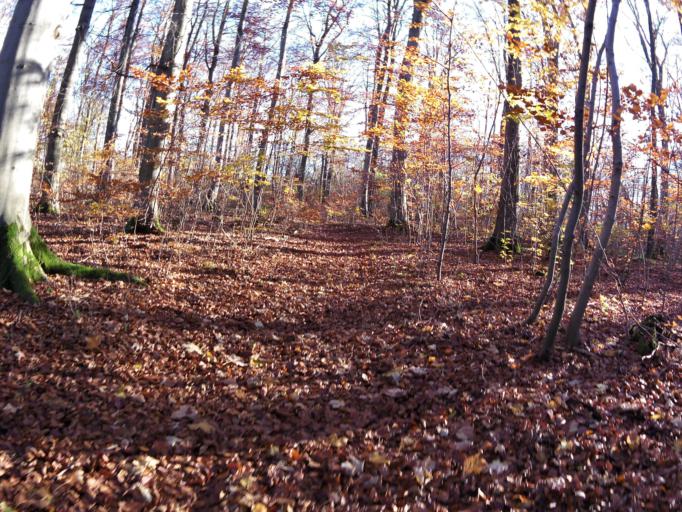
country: DE
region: Thuringia
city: Kammerforst
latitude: 51.0600
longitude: 10.4458
